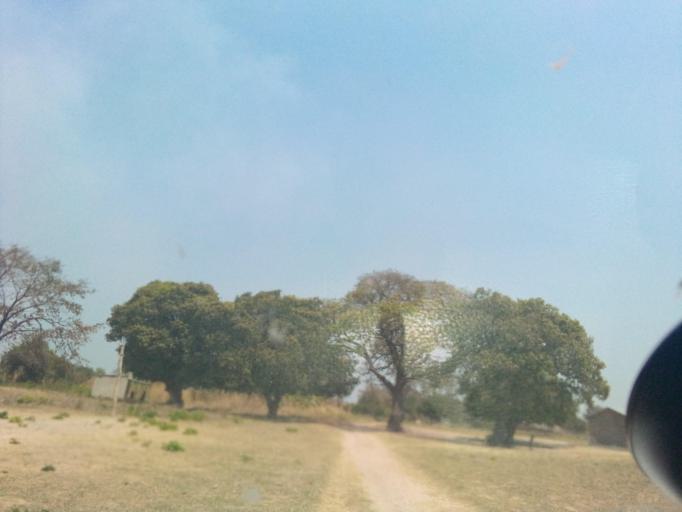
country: ZM
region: Copperbelt
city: Kataba
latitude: -12.2440
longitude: 30.3263
